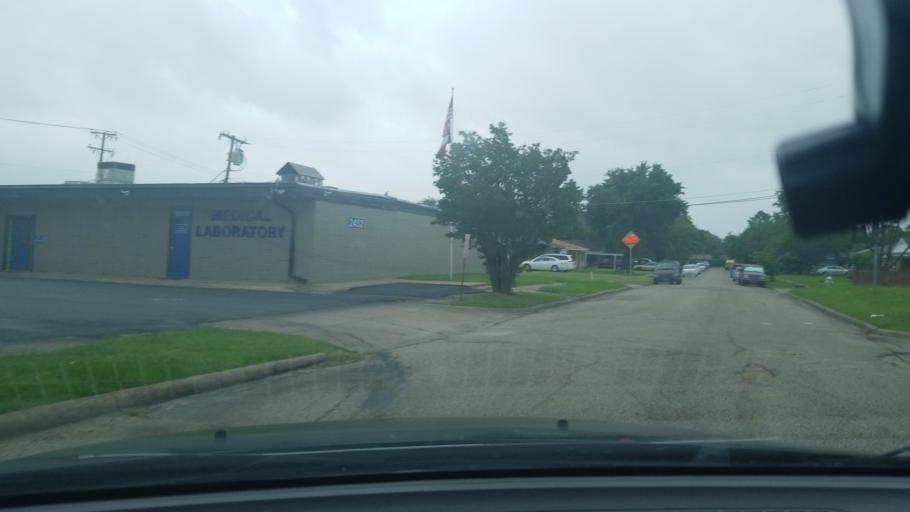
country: US
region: Texas
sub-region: Dallas County
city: Mesquite
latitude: 32.7919
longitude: -96.6359
